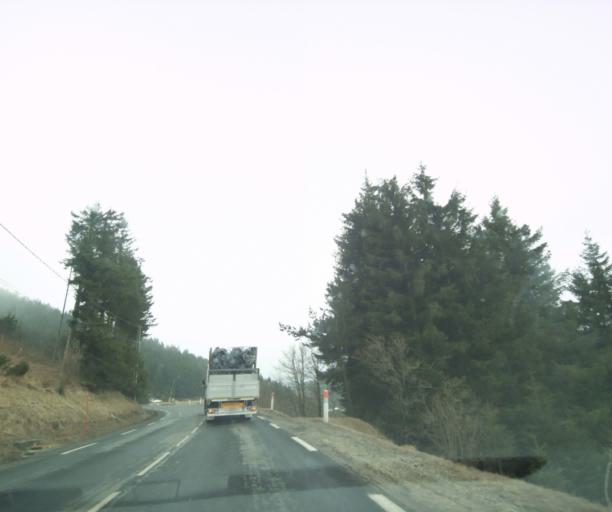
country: FR
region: Languedoc-Roussillon
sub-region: Departement de la Lozere
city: Langogne
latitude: 44.7176
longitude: 4.0074
